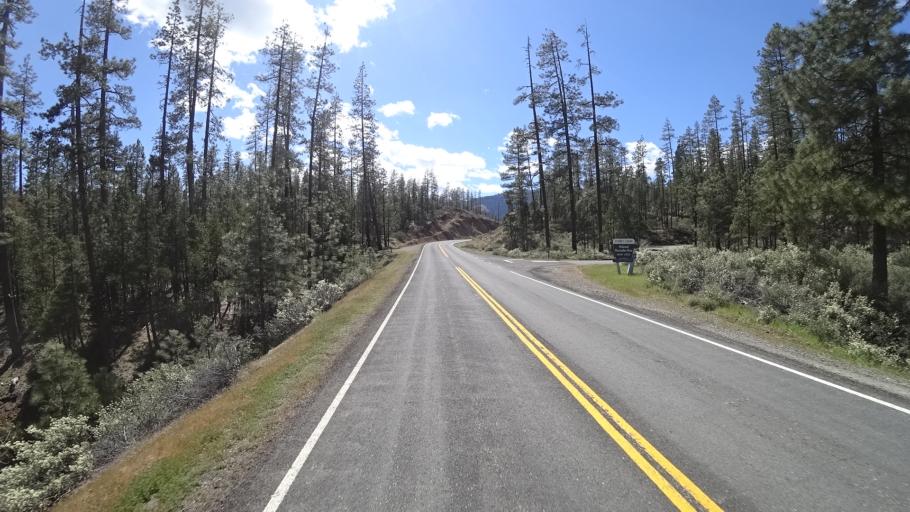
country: US
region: California
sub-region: Trinity County
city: Weaverville
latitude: 40.8502
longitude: -122.8519
